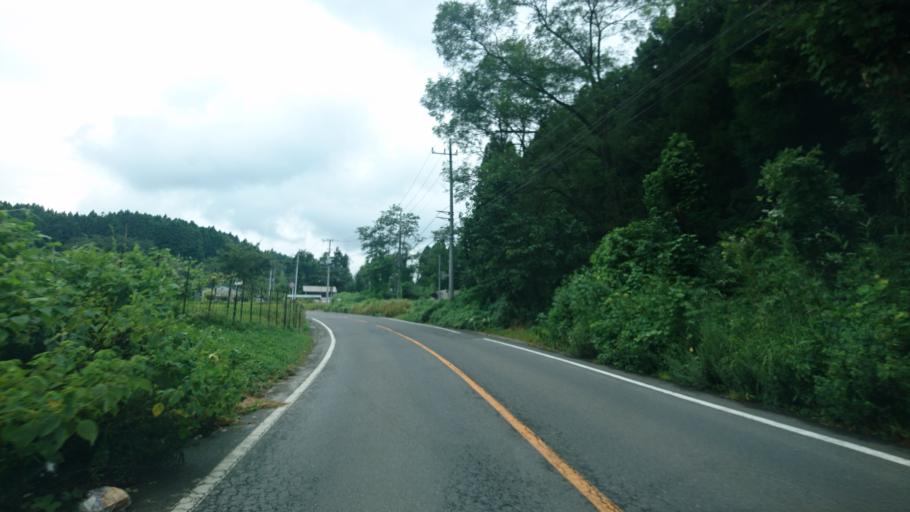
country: JP
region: Gunma
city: Omamacho-omama
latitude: 36.5024
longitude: 139.2648
